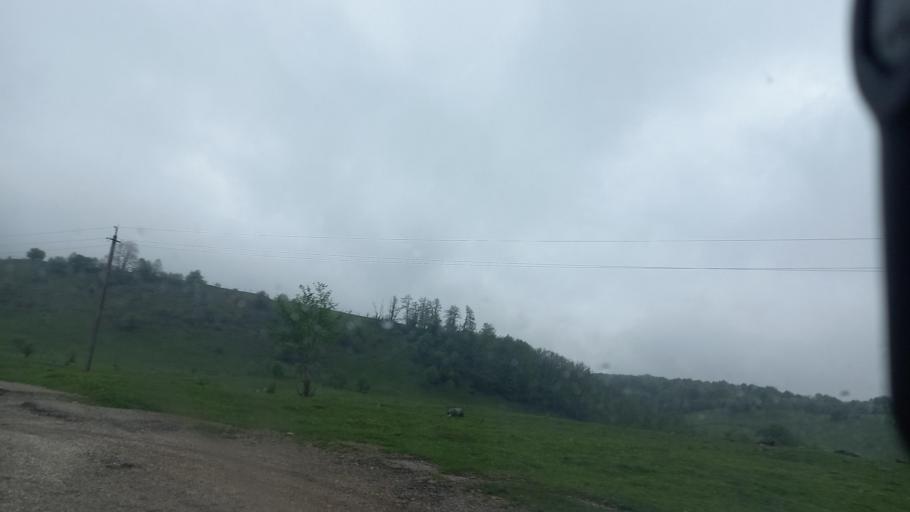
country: RU
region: Kabardino-Balkariya
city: Babugent
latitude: 43.2511
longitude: 43.5331
